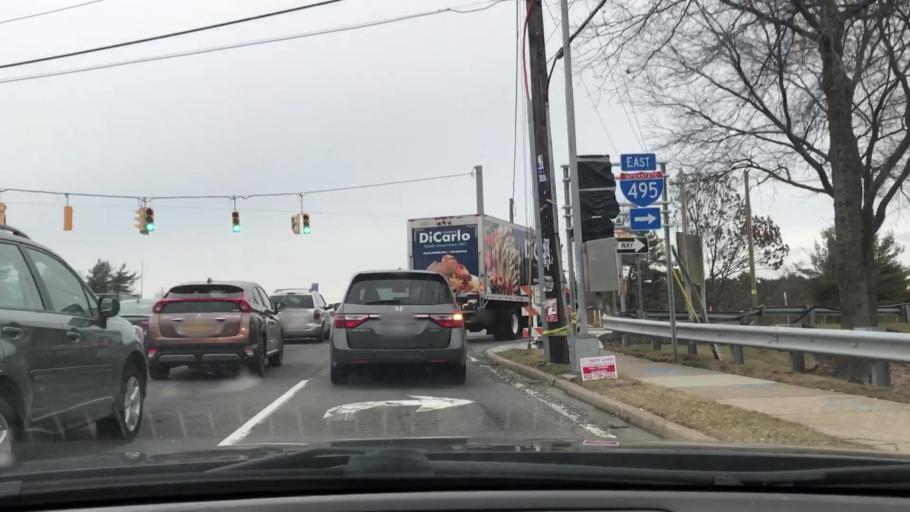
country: US
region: New York
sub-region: Suffolk County
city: Farmingville
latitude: 40.8221
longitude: -73.0199
